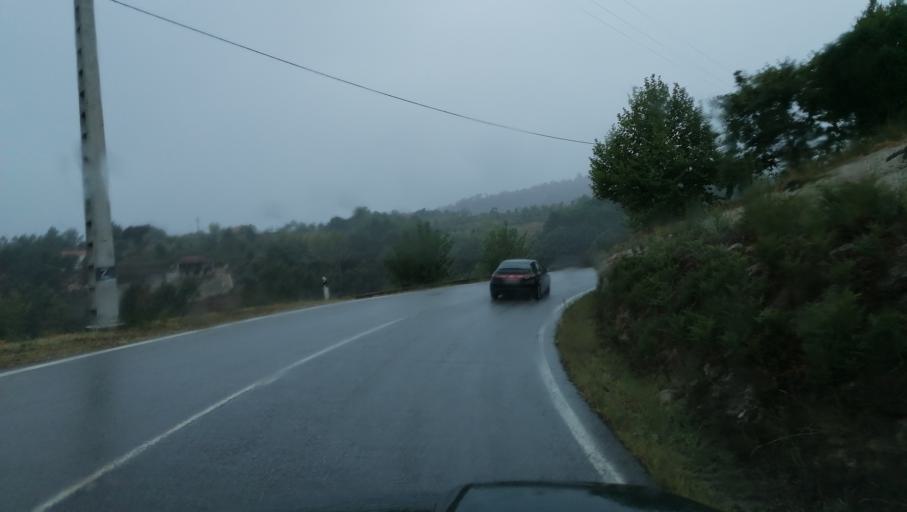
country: PT
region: Braga
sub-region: Cabeceiras de Basto
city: Cabeceiras de Basto
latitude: 41.4987
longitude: -7.9056
